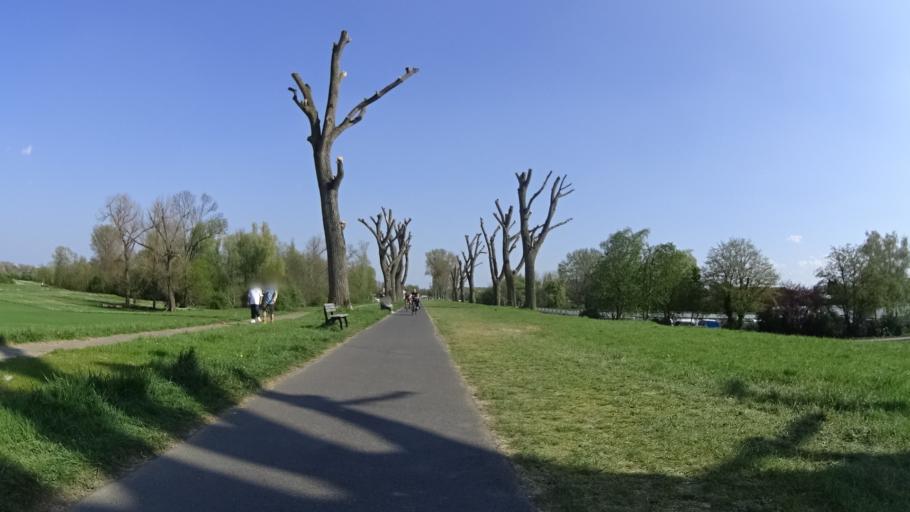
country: DE
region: North Rhine-Westphalia
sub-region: Regierungsbezirk Dusseldorf
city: Meerbusch
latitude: 51.2528
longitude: 6.7238
